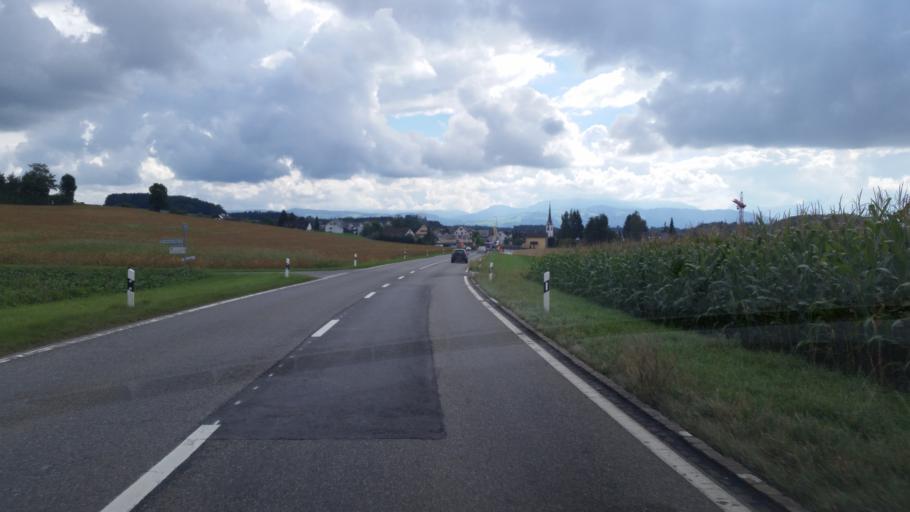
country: CH
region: Zurich
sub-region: Bezirk Affoltern
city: Mettmenstetten
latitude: 47.2504
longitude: 8.4573
